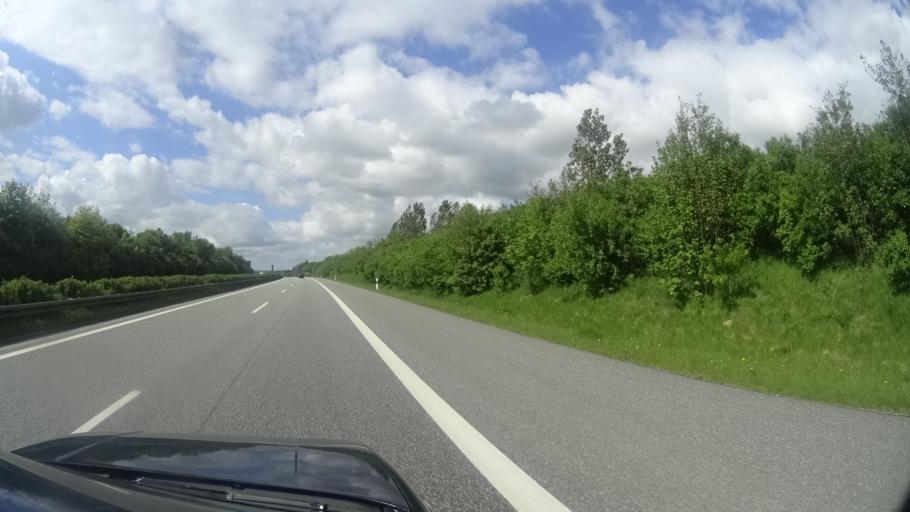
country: DE
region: Mecklenburg-Vorpommern
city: Laage
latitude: 53.8300
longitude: 12.2992
